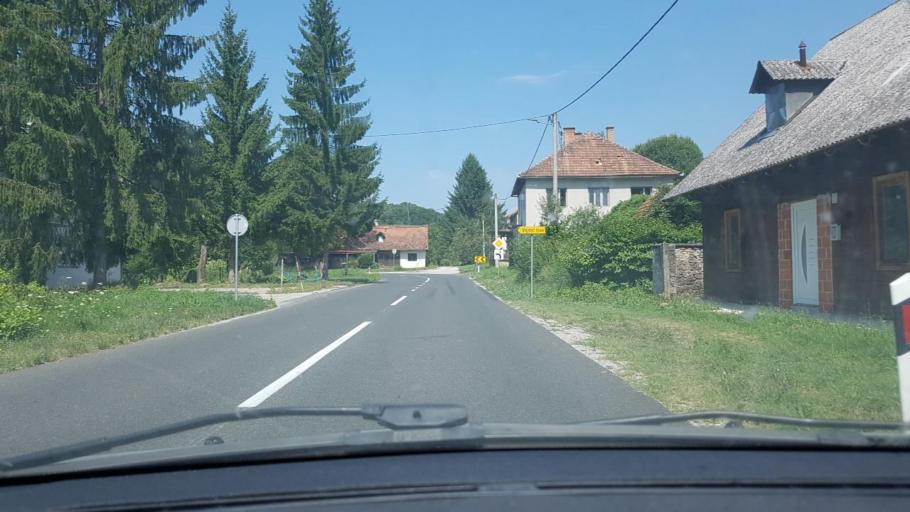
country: HR
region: Karlovacka
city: Vojnic
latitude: 45.2433
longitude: 15.7310
